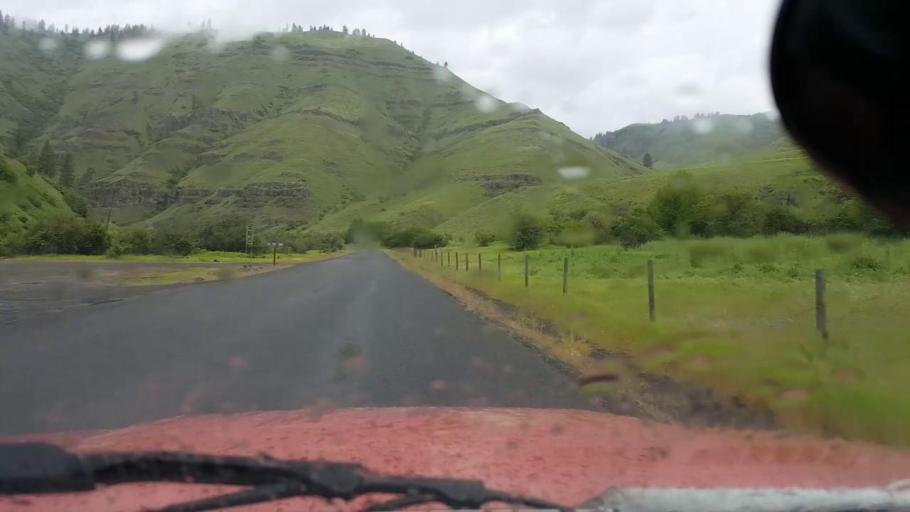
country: US
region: Washington
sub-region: Asotin County
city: Asotin
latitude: 46.0303
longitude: -117.3162
